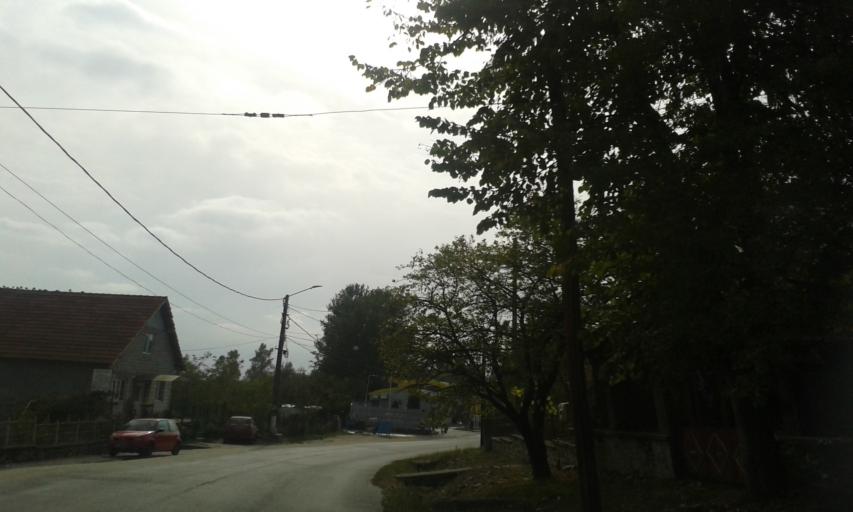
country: RO
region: Gorj
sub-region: Comuna Targu Carbunesti
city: Targu Carbunesti
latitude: 44.9511
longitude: 23.5140
